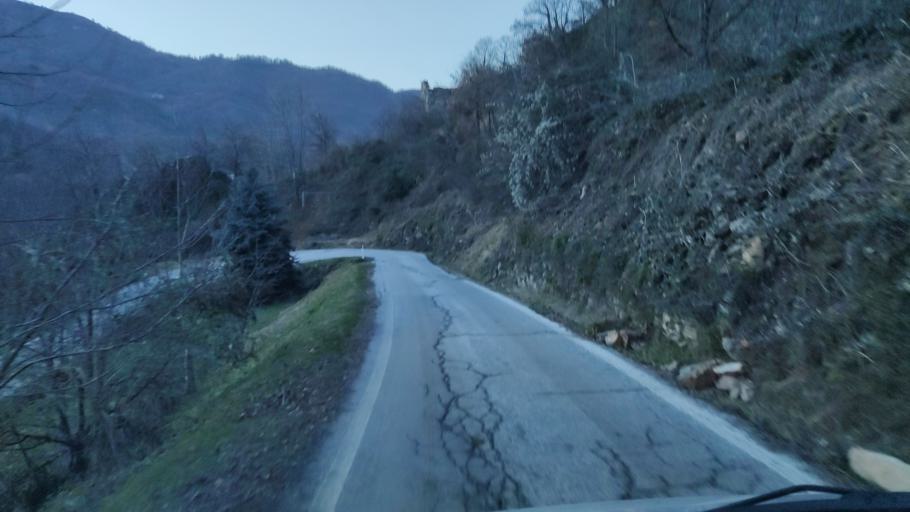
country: IT
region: Piedmont
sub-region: Provincia di Cuneo
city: Lisio
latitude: 44.2938
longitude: 7.9817
